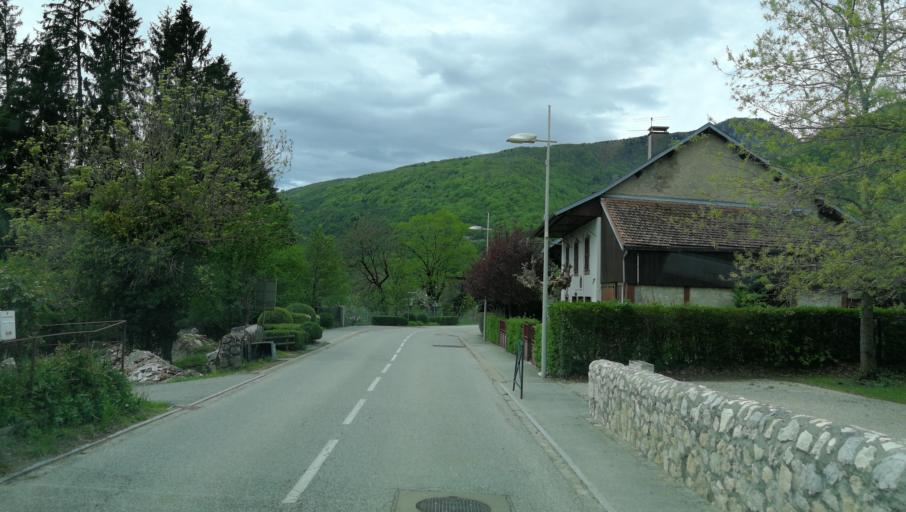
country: FR
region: Rhone-Alpes
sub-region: Departement de l'Ain
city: Bellegarde-sur-Valserine
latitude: 46.0044
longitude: 5.7847
